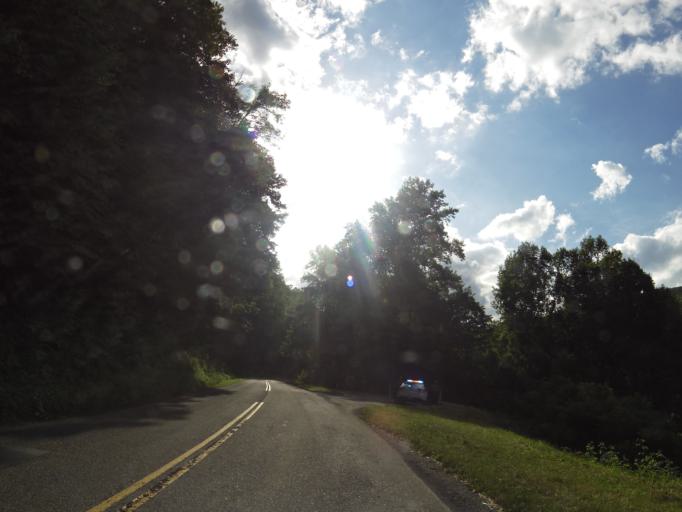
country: US
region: Tennessee
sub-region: Sevier County
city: Gatlinburg
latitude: 35.6727
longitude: -83.5709
